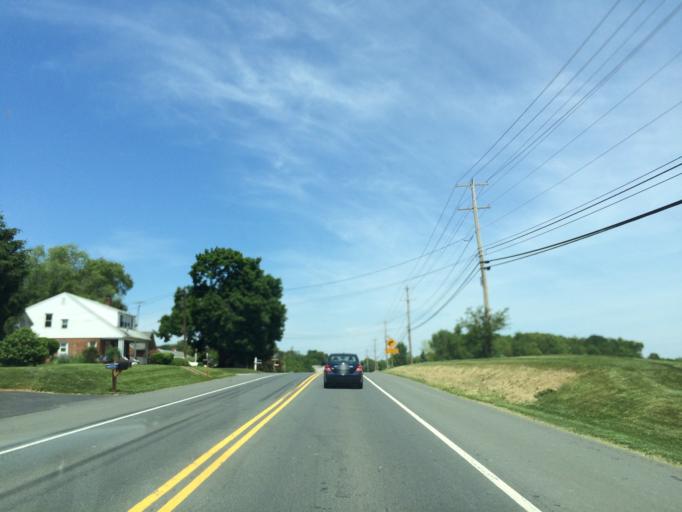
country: US
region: Maryland
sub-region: Washington County
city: Saint James
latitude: 39.5862
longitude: -77.7305
